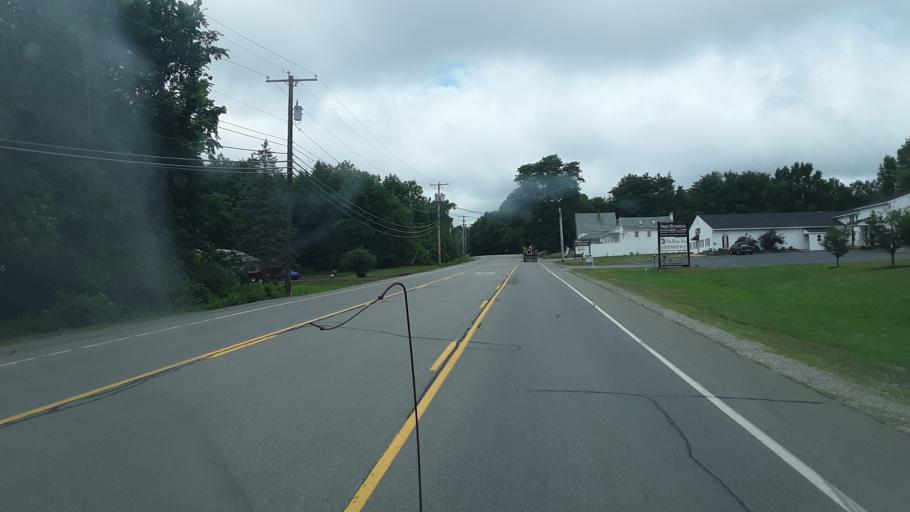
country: US
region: New Hampshire
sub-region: Rockingham County
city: Northwood
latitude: 43.2055
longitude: -71.1699
